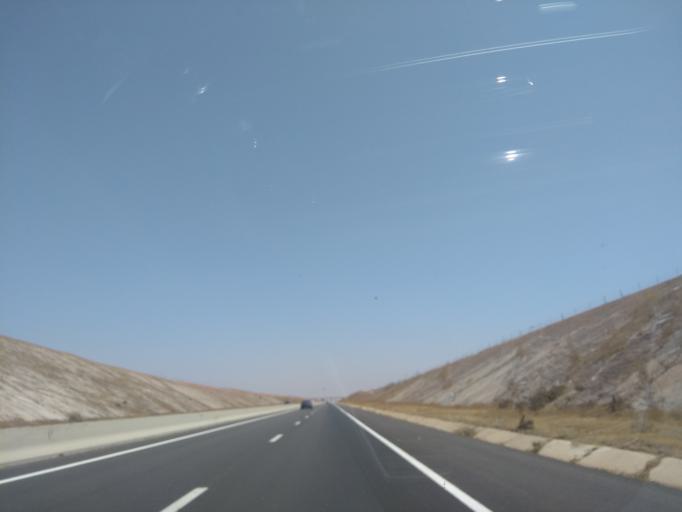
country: MA
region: Marrakech-Tensift-Al Haouz
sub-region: Kelaa-Des-Sraghna
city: Sidi Abdallah
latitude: 32.3107
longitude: -7.9589
